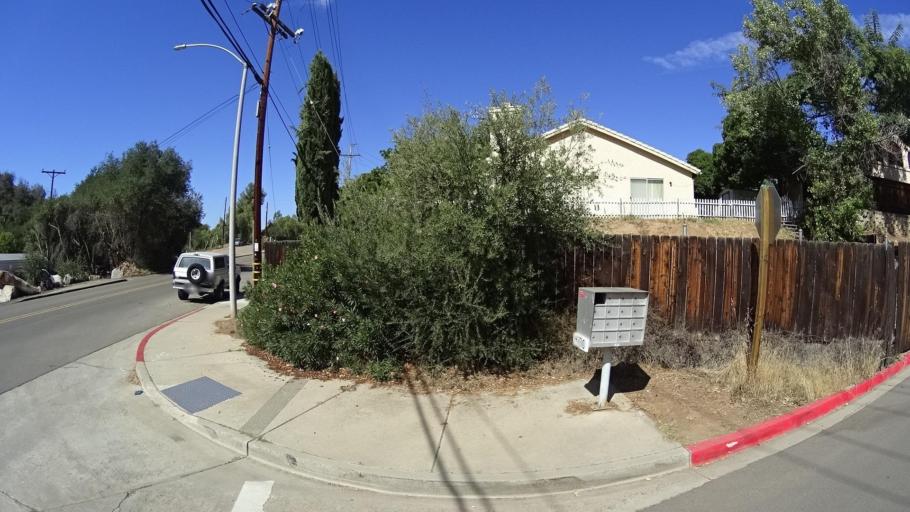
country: US
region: California
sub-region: San Diego County
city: Crest
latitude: 32.8393
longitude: -116.8749
